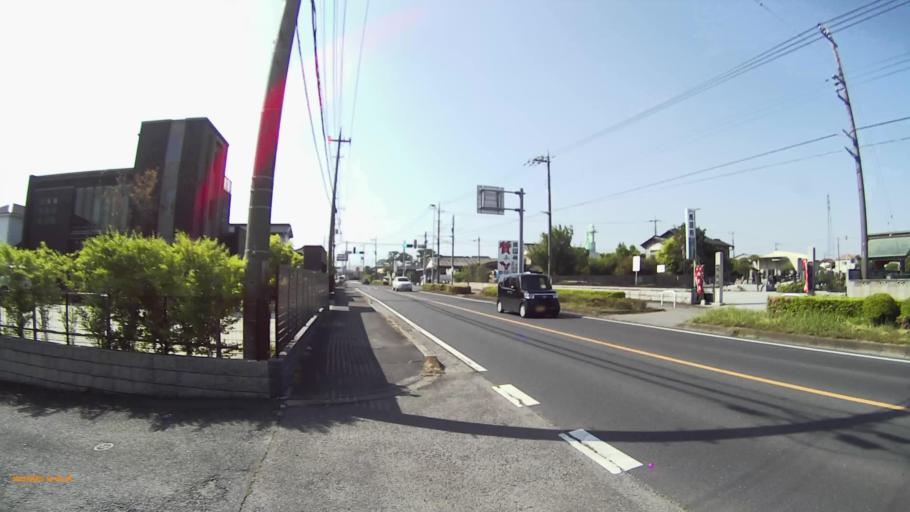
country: JP
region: Saitama
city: Sugito
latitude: 36.0167
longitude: 139.7504
